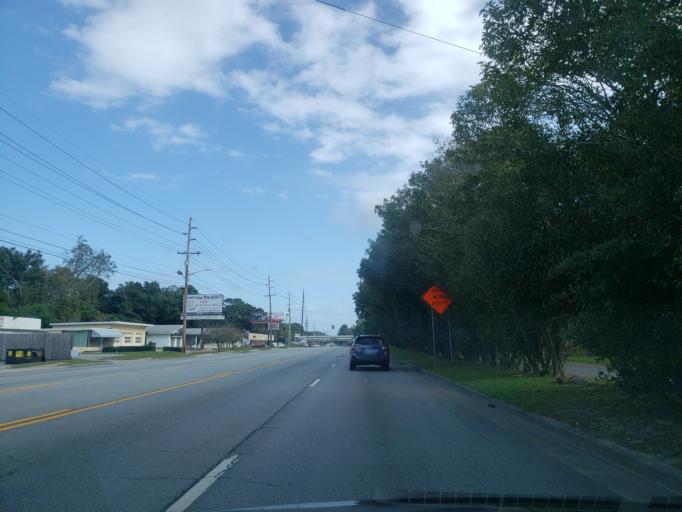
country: US
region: Georgia
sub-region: Chatham County
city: Thunderbolt
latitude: 32.0239
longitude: -81.0928
